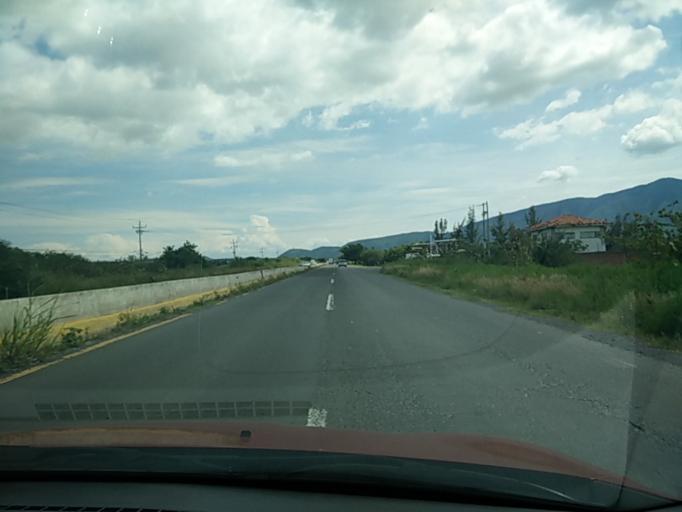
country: MX
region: Jalisco
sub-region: Ixtlahuacan de los Membrillos
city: Los Cedros
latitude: 20.4073
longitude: -103.2304
